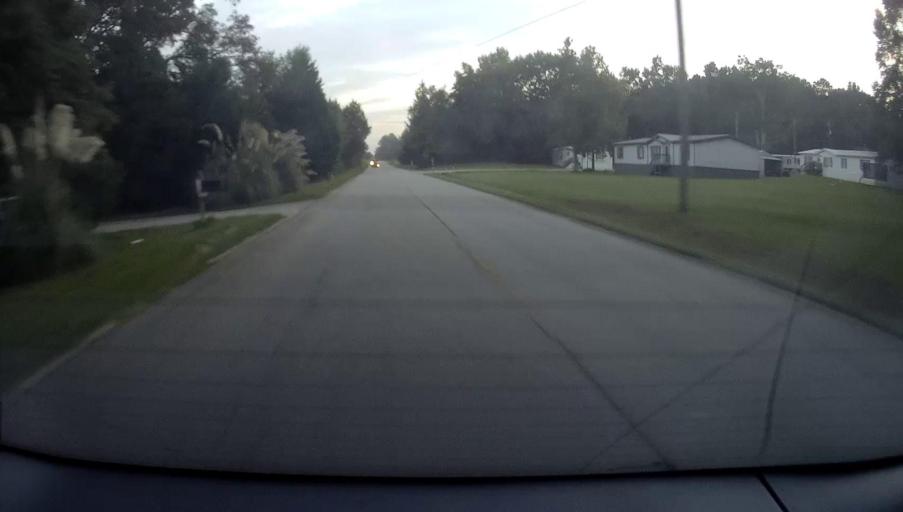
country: US
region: Georgia
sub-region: Henry County
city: Locust Grove
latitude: 33.3086
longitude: -84.0430
